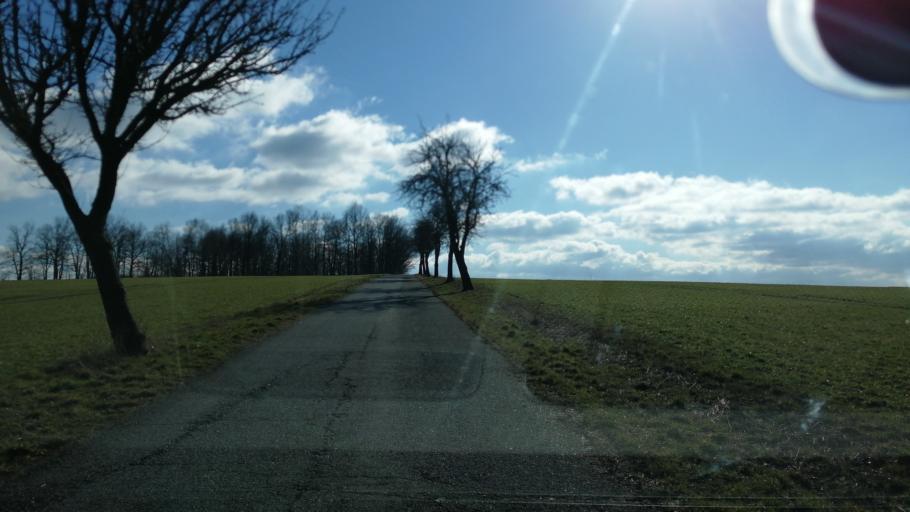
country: DE
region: Saxony
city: Weissenberg
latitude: 51.1617
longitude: 14.7205
